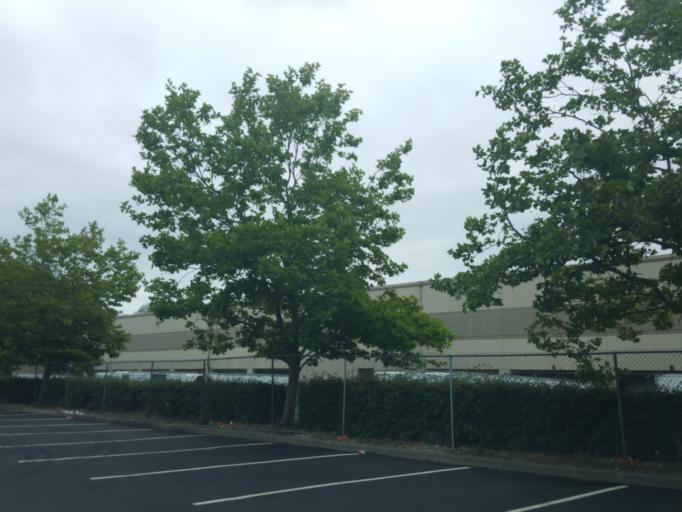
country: US
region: Washington
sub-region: Pierce County
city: Lakewood
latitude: 47.1696
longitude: -122.5034
